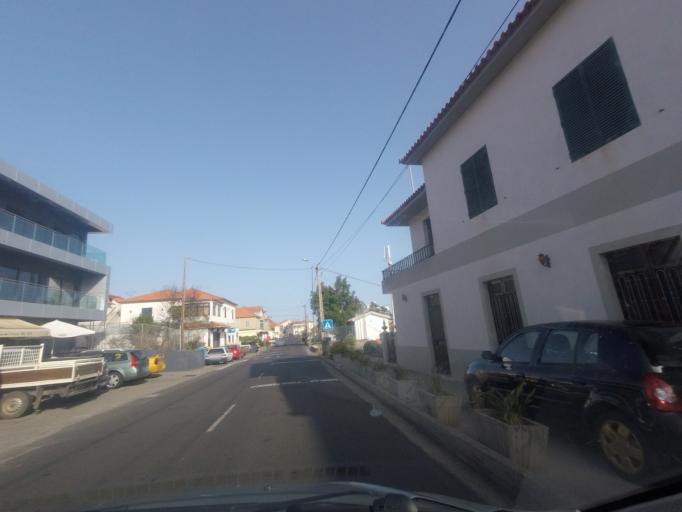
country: PT
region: Madeira
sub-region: Calheta
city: Arco da Calheta
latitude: 32.6979
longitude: -17.1195
